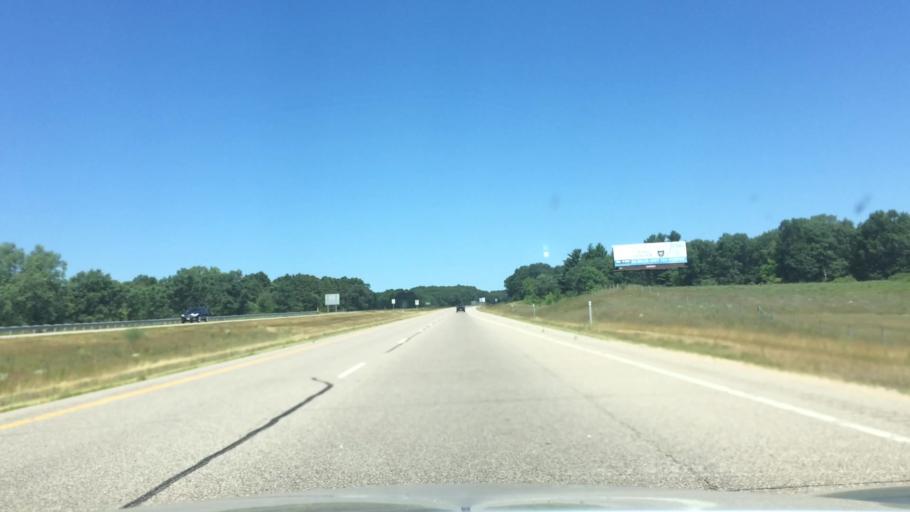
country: US
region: Wisconsin
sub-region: Marquette County
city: Westfield
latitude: 44.0399
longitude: -89.5330
